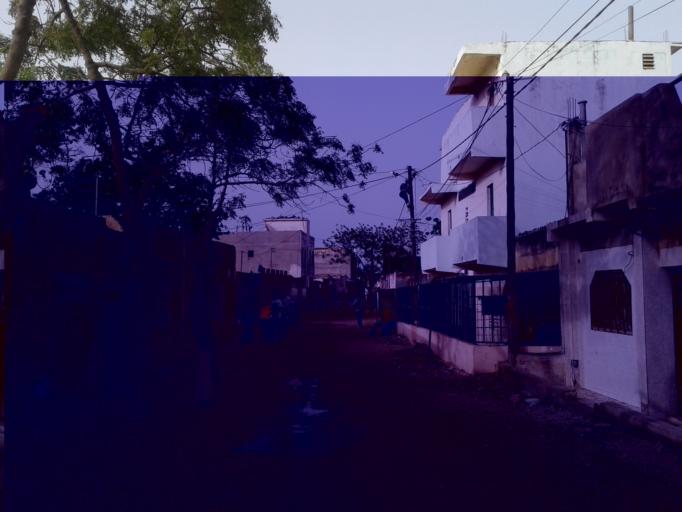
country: SN
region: Dakar
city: Pikine
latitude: 14.7657
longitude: -17.3787
